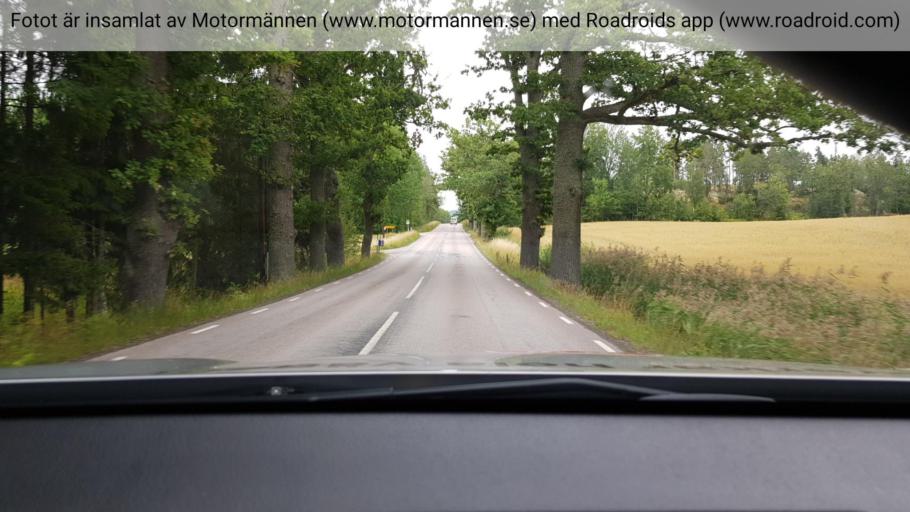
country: SE
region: Soedermanland
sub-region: Gnesta Kommun
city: Gnesta
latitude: 59.0856
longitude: 17.2595
